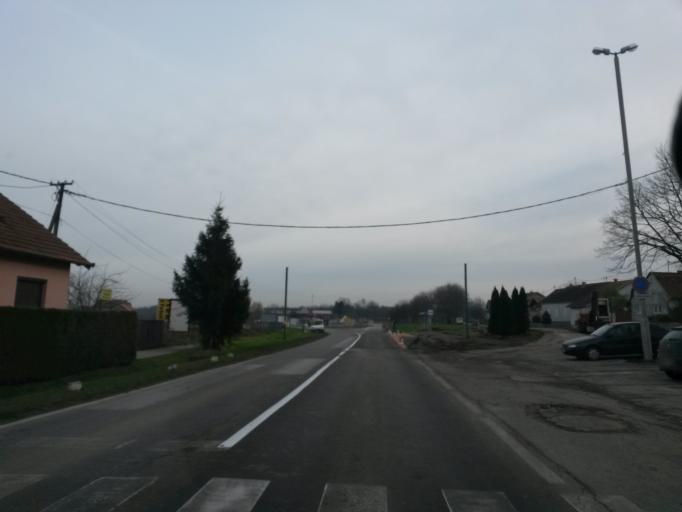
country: HR
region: Vukovarsko-Srijemska
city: Nustar
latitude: 45.3336
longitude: 18.8505
